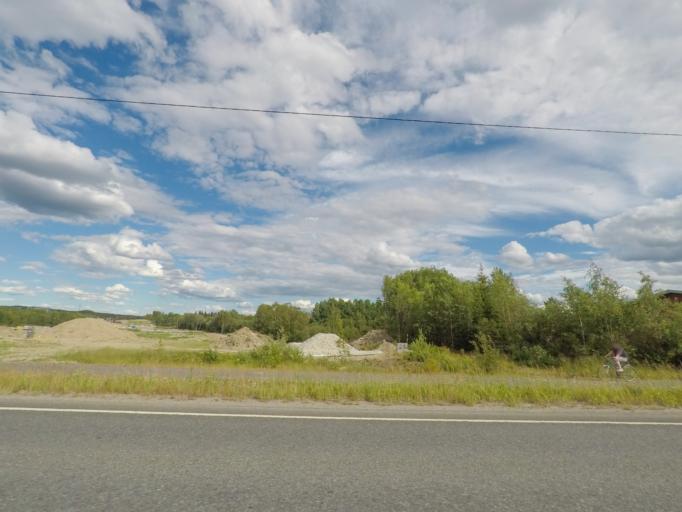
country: FI
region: Paijanne Tavastia
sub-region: Lahti
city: Lahti
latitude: 60.9543
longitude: 25.6162
